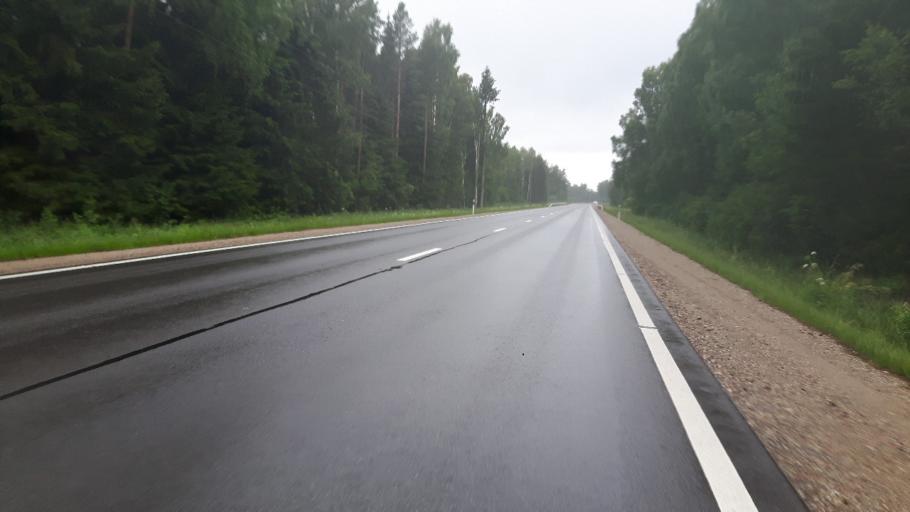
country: LV
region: Rucavas
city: Rucava
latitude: 56.2258
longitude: 21.1171
